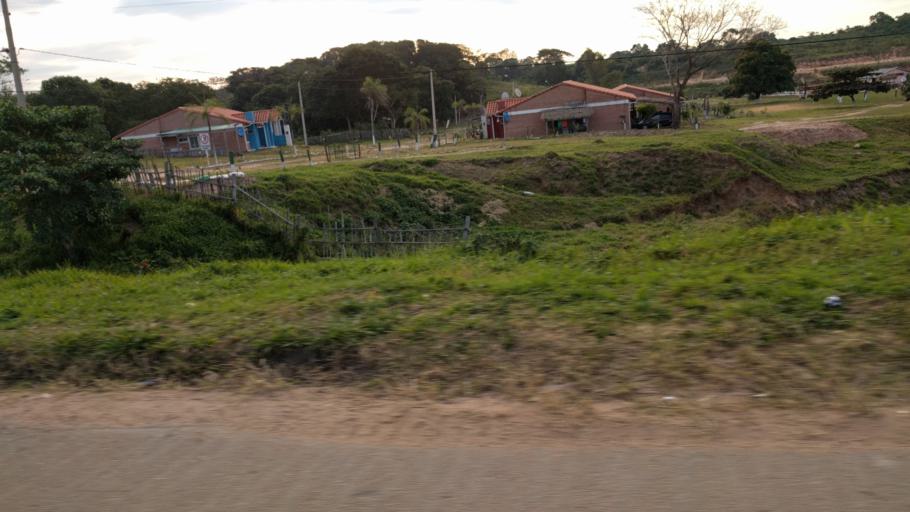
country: BO
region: Santa Cruz
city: Buena Vista
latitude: -17.4541
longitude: -63.6557
